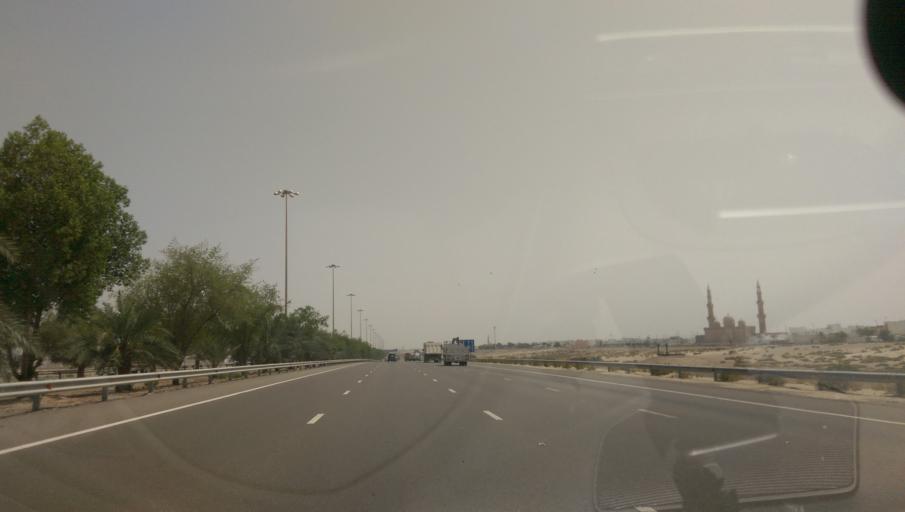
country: AE
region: Abu Dhabi
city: Abu Dhabi
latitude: 24.3480
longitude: 54.6421
